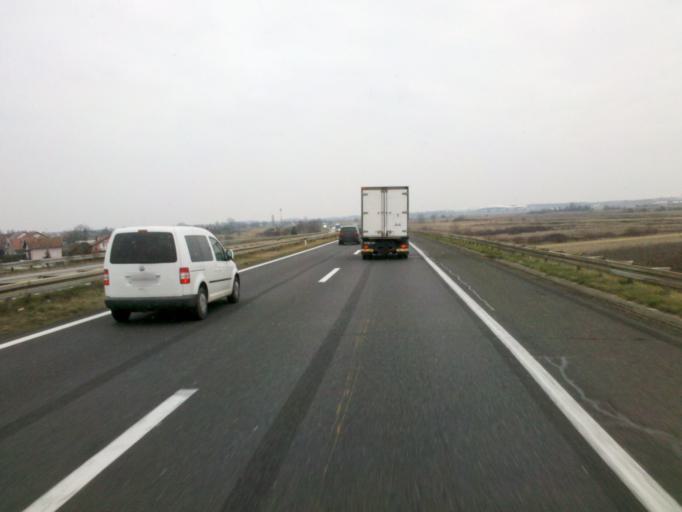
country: HR
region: Zagrebacka
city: Micevec
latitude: 45.7461
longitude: 16.0436
